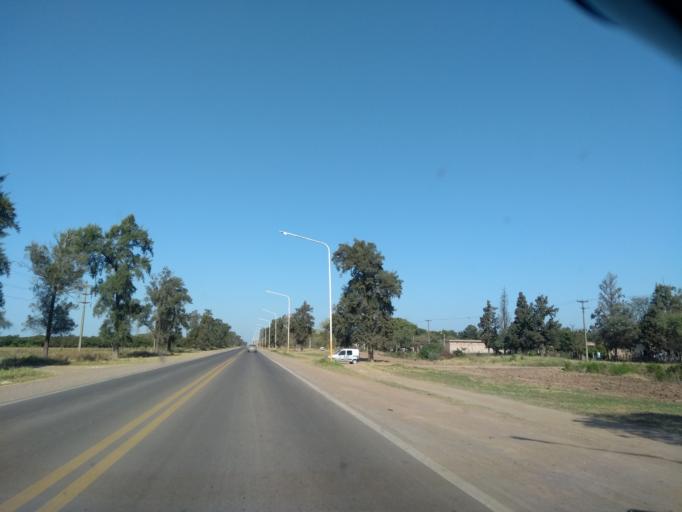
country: AR
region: Chaco
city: Presidencia Roque Saenz Pena
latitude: -26.7895
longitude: -60.4083
